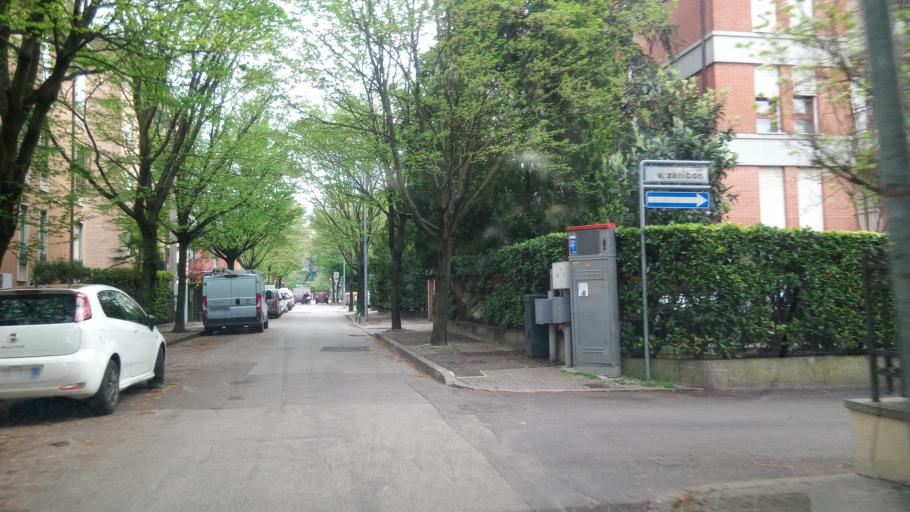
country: IT
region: Veneto
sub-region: Provincia di Padova
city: Padova
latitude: 45.4128
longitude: 11.8607
